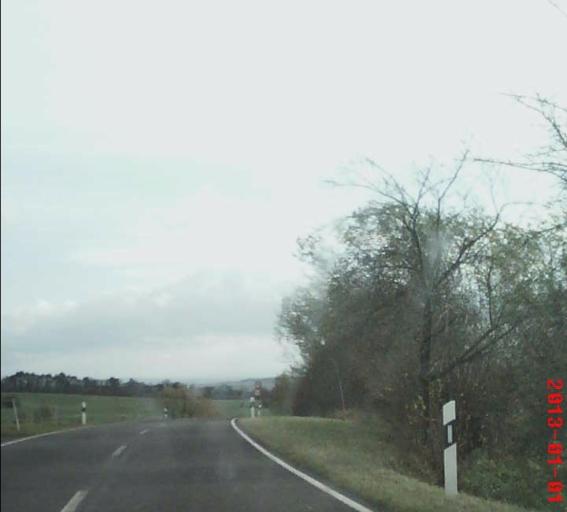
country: DE
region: Thuringia
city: Kullstedt
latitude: 51.2718
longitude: 10.2836
